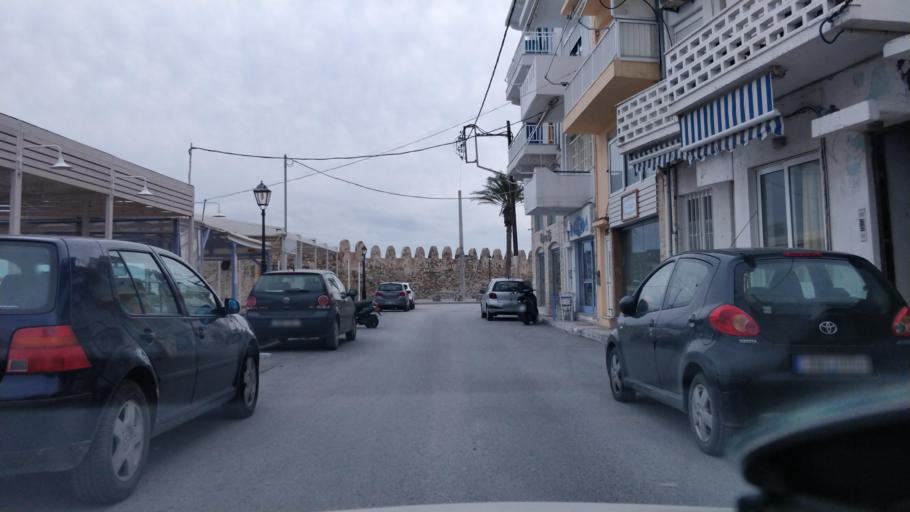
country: GR
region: Crete
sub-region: Nomos Lasithiou
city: Ierapetra
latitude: 35.0047
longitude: 25.7375
